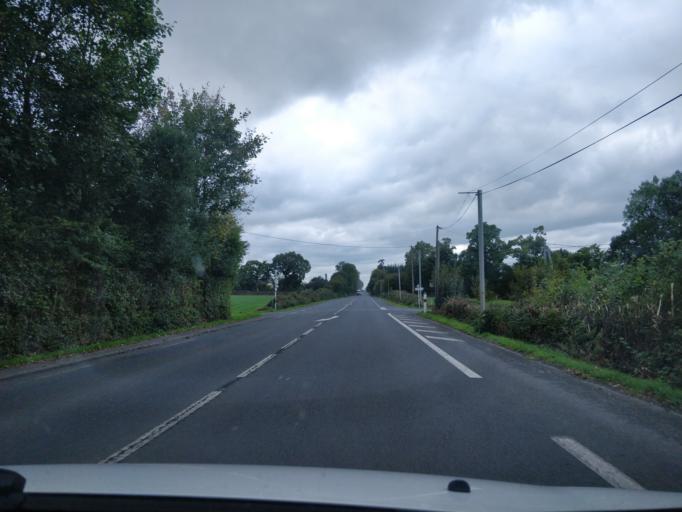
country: FR
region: Lower Normandy
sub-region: Departement du Calvados
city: Saint-Sever-Calvados
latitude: 48.8278
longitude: -1.0889
